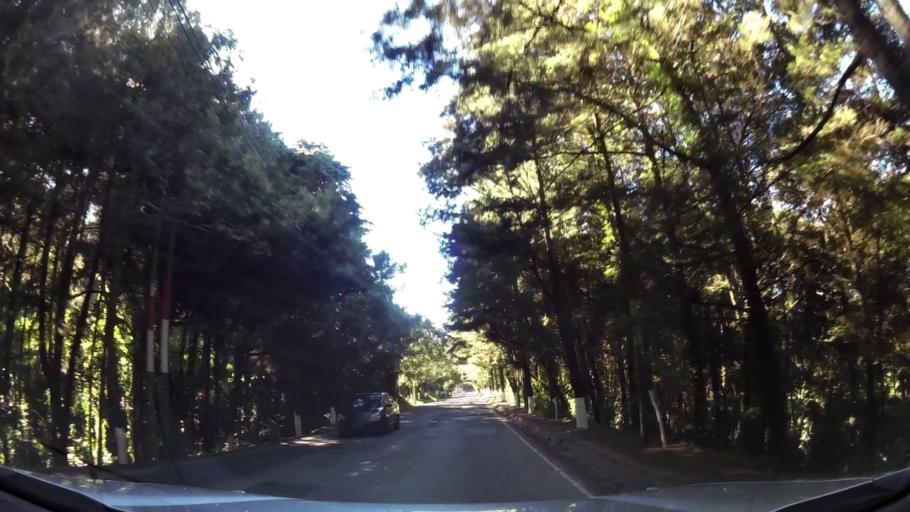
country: GT
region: Guatemala
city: Santa Catarina Pinula
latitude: 14.5188
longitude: -90.4665
